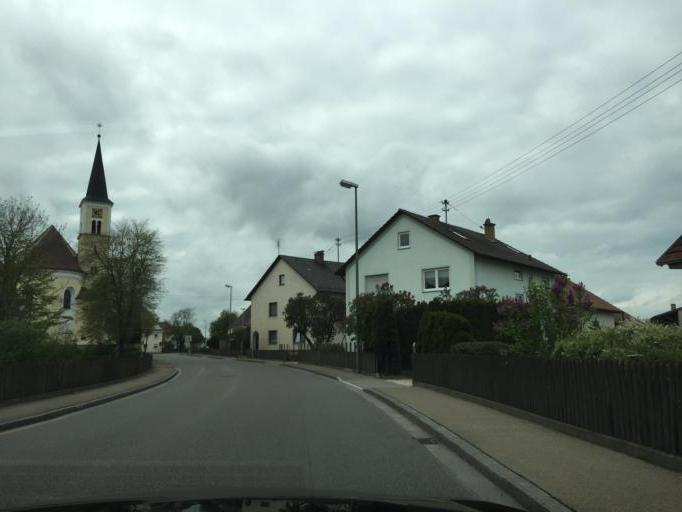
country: DE
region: Bavaria
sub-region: Swabia
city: Binswangen
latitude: 48.5681
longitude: 10.6005
